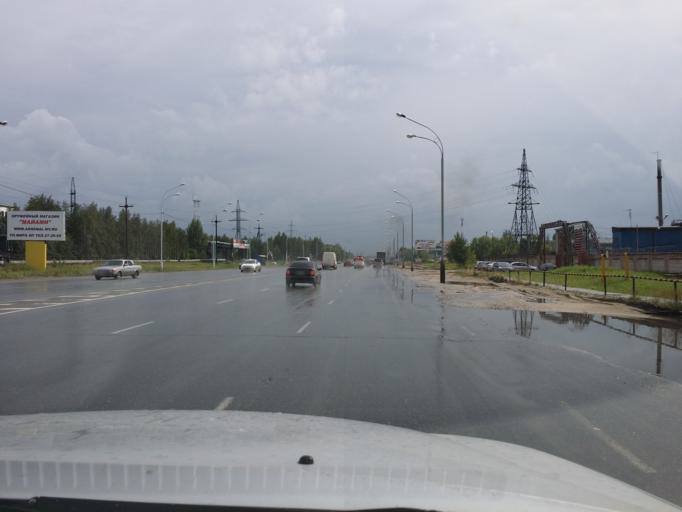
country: RU
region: Khanty-Mansiyskiy Avtonomnyy Okrug
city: Nizhnevartovsk
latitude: 60.9468
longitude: 76.5294
